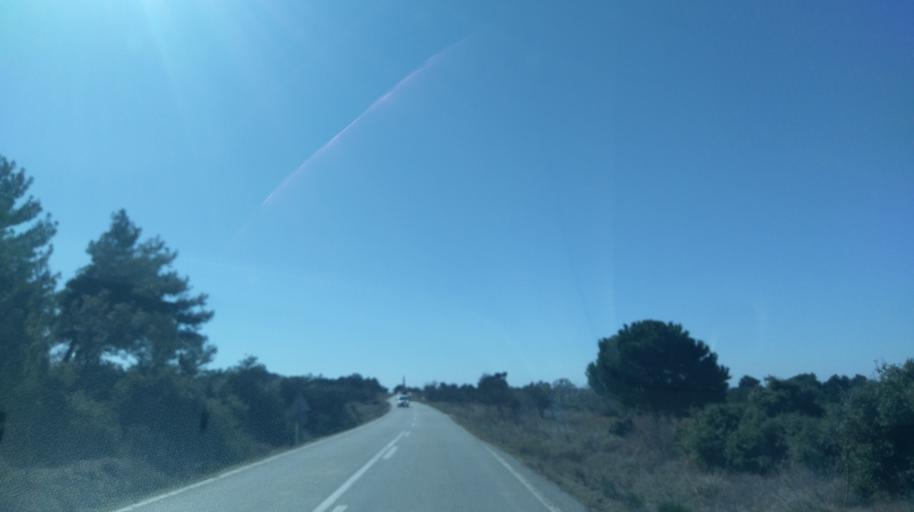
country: TR
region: Canakkale
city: Intepe
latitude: 40.1037
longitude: 26.2315
